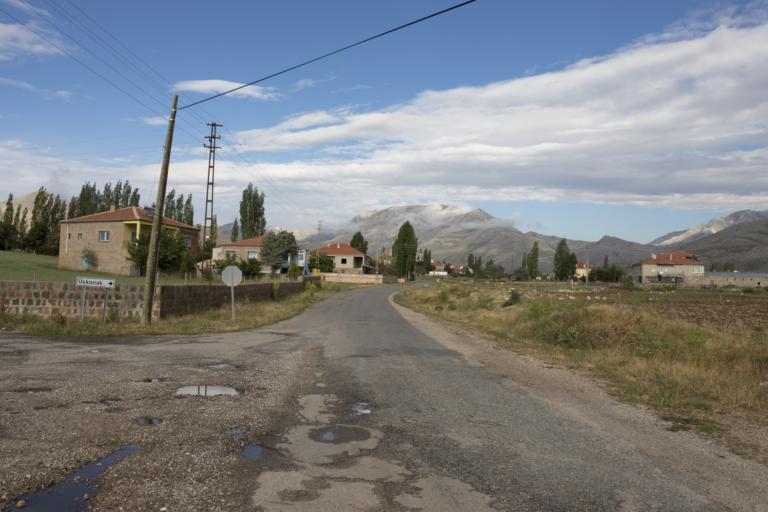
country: TR
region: Kayseri
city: Toklar
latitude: 38.4070
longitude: 36.0729
